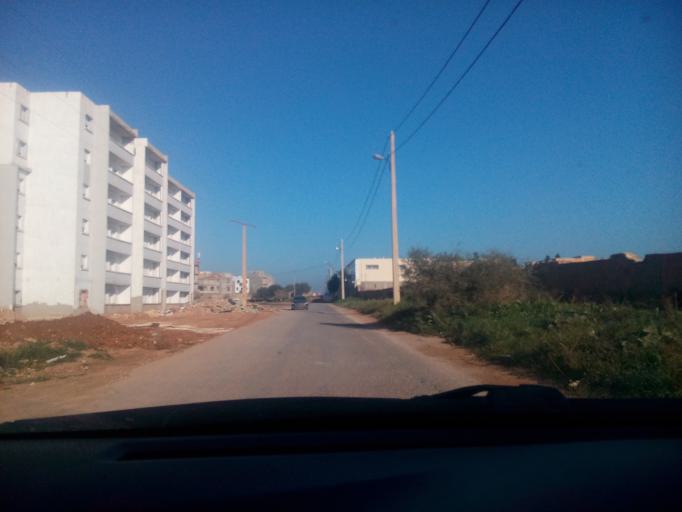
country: DZ
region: Oran
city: Bir el Djir
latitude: 35.7542
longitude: -0.5299
